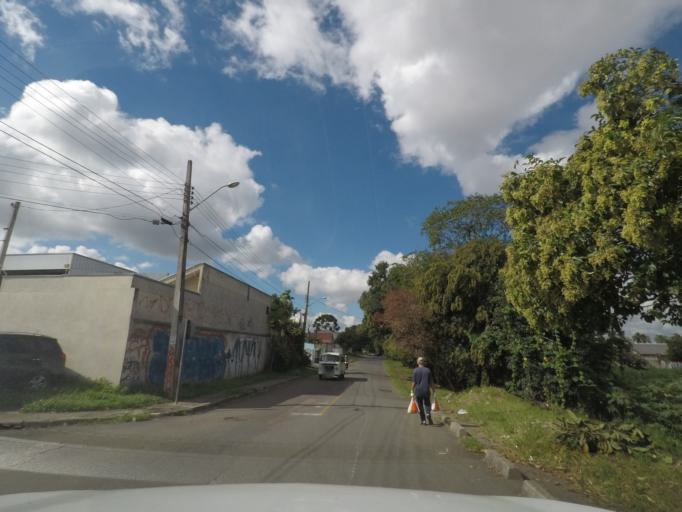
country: BR
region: Parana
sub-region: Sao Jose Dos Pinhais
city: Sao Jose dos Pinhais
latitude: -25.4848
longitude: -49.2352
